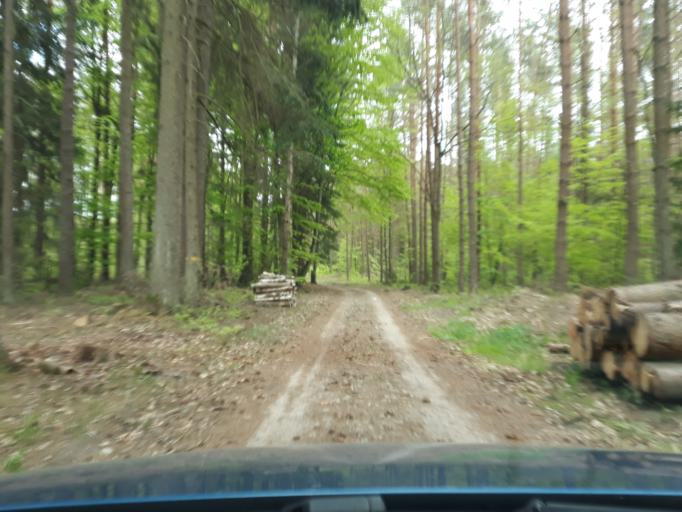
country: PL
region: Pomeranian Voivodeship
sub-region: Powiat czluchowski
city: Czluchow
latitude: 53.7561
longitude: 17.3497
